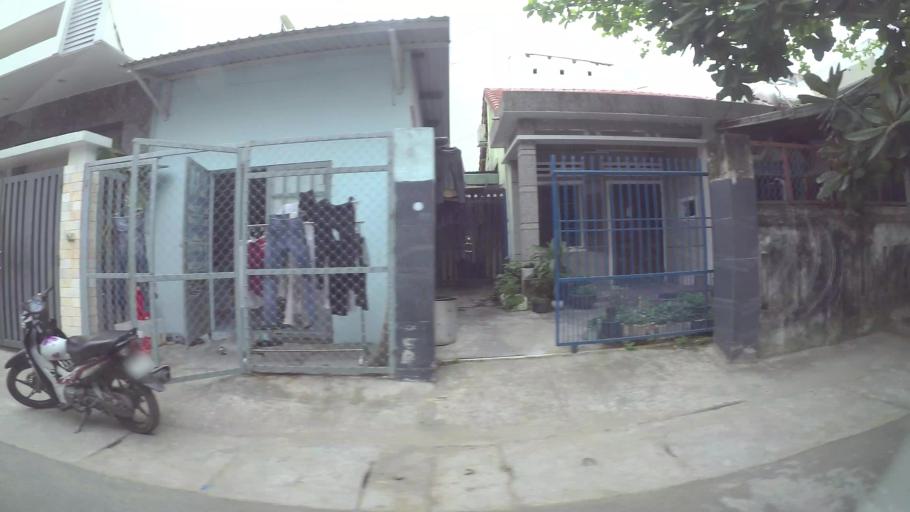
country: VN
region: Da Nang
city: Thanh Khe
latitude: 16.0679
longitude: 108.1855
